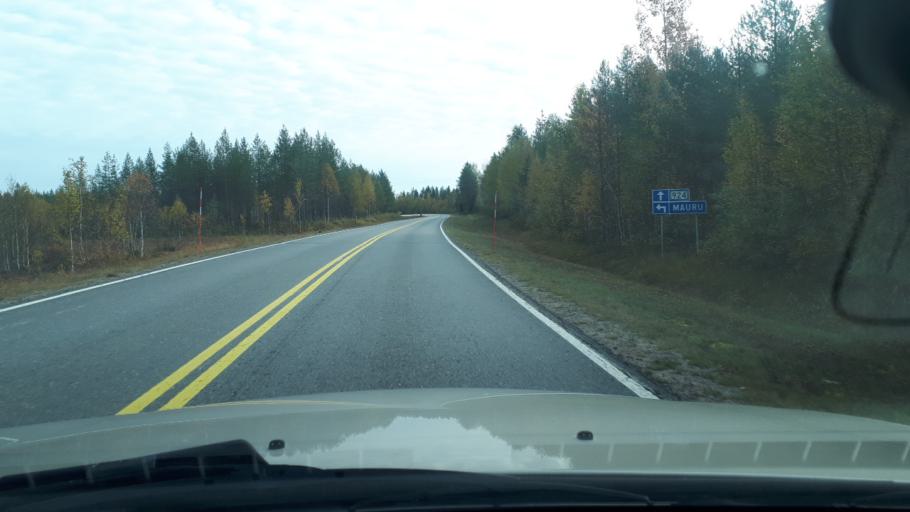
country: FI
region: Lapland
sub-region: Rovaniemi
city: Ranua
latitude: 65.9634
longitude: 25.9668
